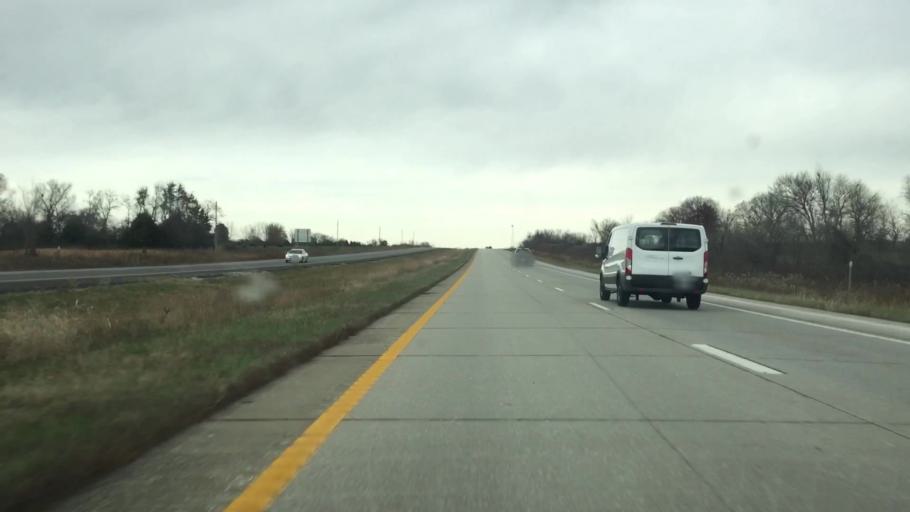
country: US
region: Missouri
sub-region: Saint Clair County
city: Osceola
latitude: 38.1135
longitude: -93.7062
